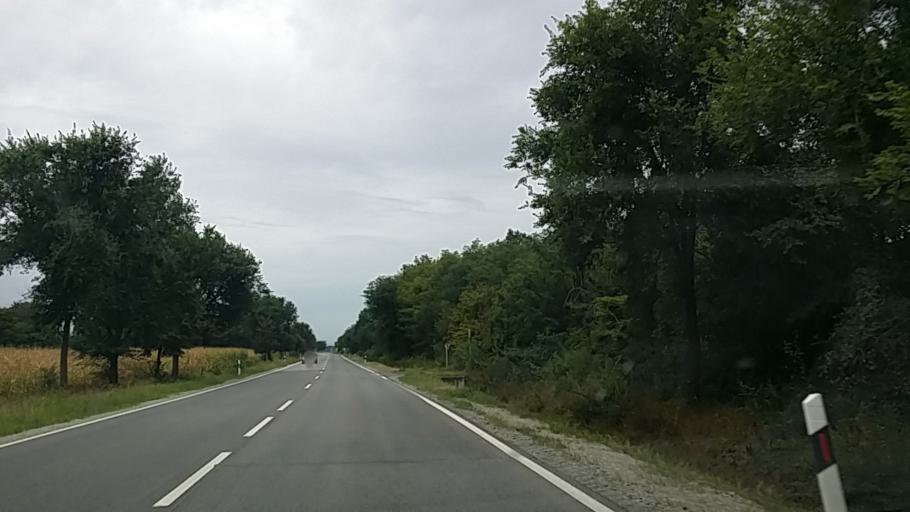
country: HU
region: Gyor-Moson-Sopron
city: Fertoszentmiklos
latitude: 47.5971
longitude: 16.8291
